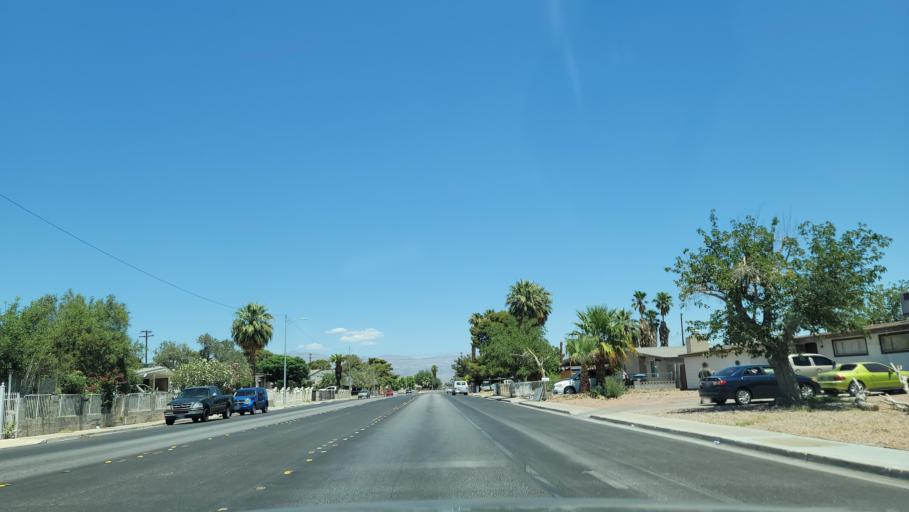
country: US
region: Nevada
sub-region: Clark County
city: Las Vegas
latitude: 36.1756
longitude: -115.1253
